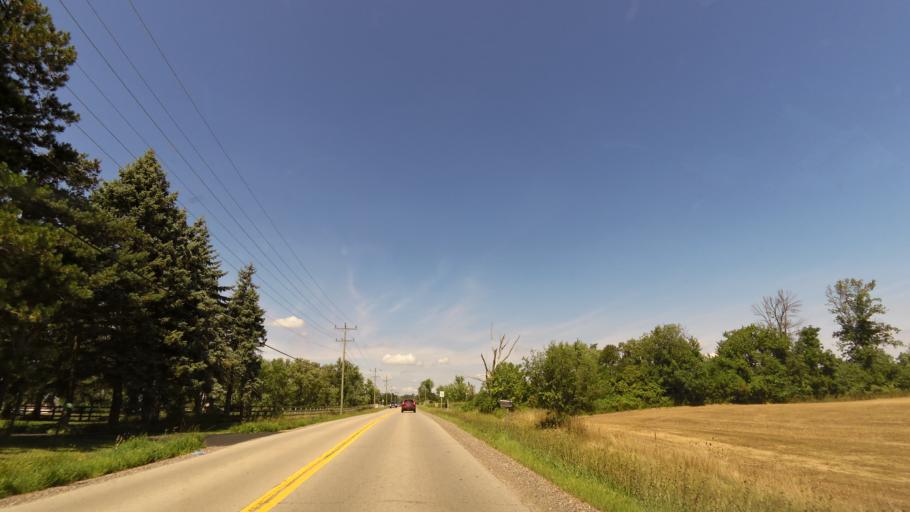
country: CA
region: Ontario
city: Ancaster
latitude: 43.1742
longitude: -79.9733
